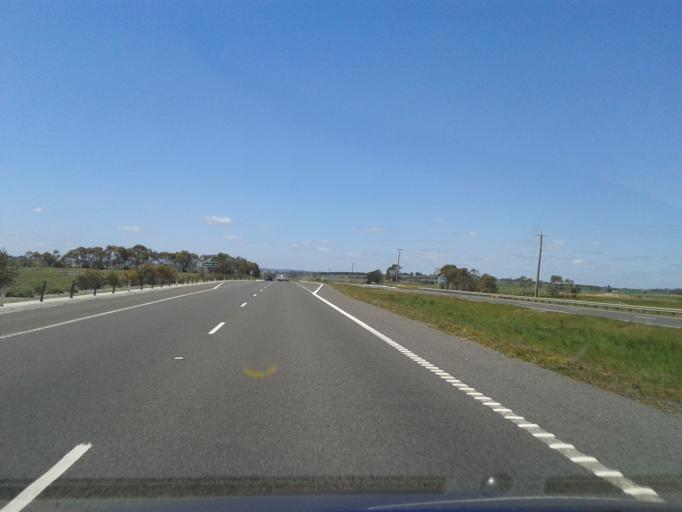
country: AU
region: Victoria
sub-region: Ballarat North
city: Newington
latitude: -37.4815
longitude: 143.7274
